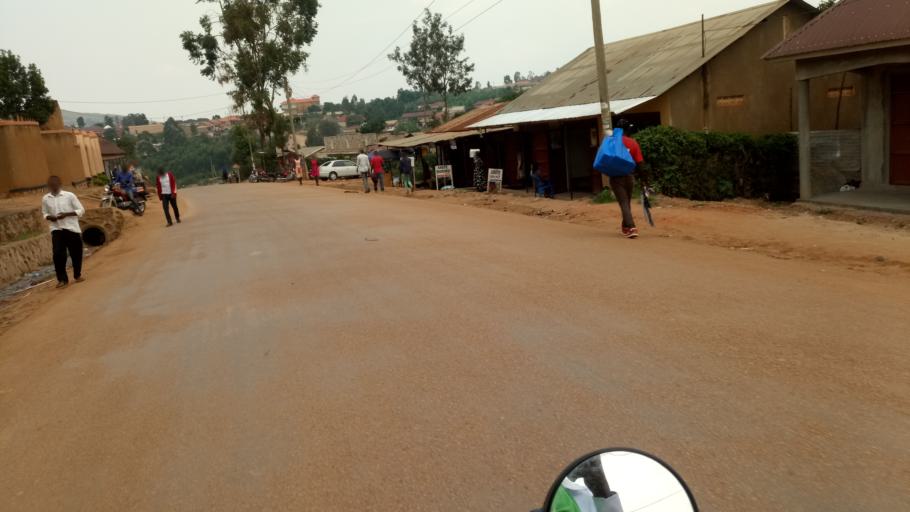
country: UG
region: Western Region
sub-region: Mbarara District
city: Mbarara
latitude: -0.6149
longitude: 30.6665
